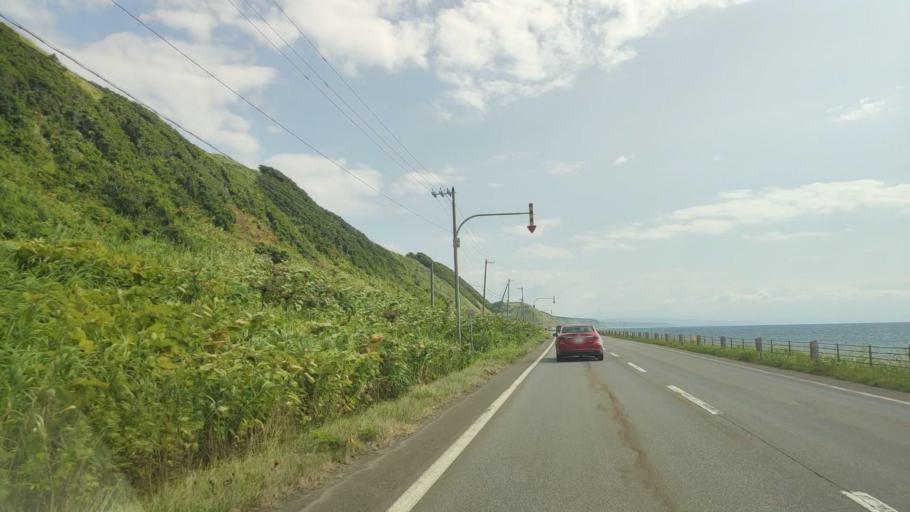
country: JP
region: Hokkaido
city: Rumoi
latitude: 44.0816
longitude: 141.6622
